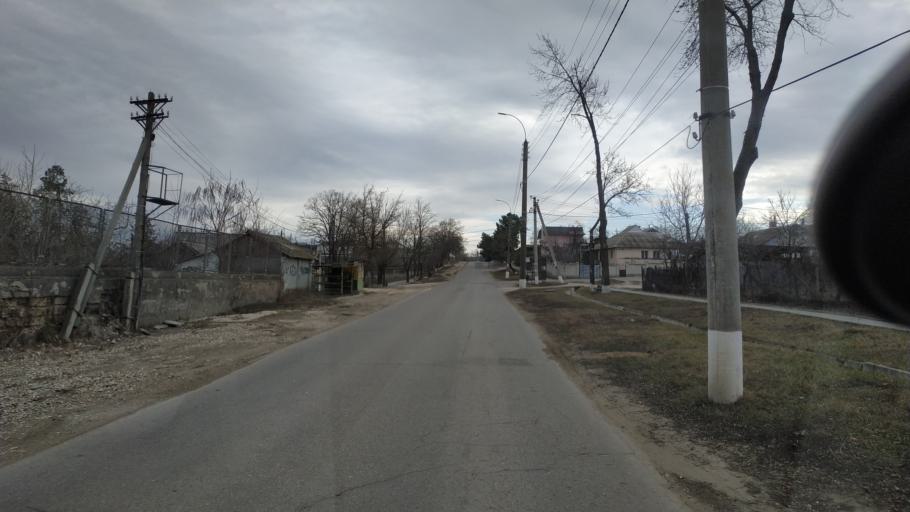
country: MD
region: Chisinau
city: Vadul lui Voda
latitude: 47.0970
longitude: 29.0707
